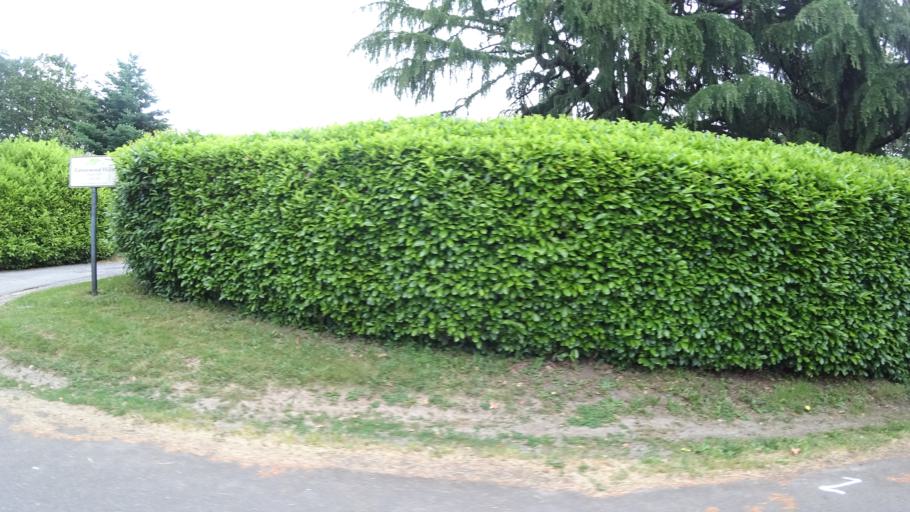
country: US
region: Oregon
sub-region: Clackamas County
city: Lake Oswego
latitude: 45.4599
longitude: -122.6823
